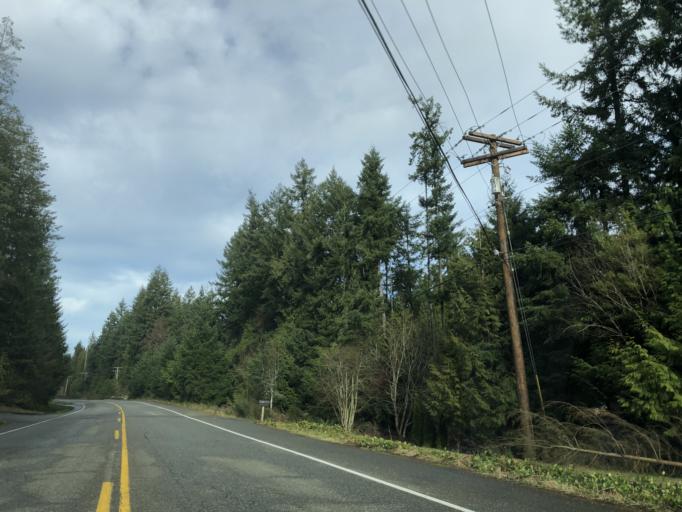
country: US
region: Washington
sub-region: Kitsap County
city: Poulsbo
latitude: 47.7634
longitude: -122.6508
